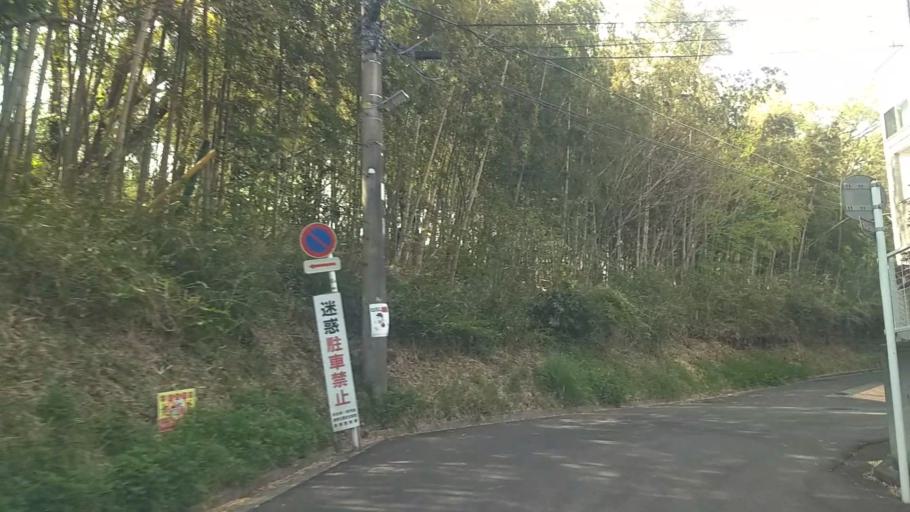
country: JP
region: Kanagawa
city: Kamakura
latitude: 35.3821
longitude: 139.5681
